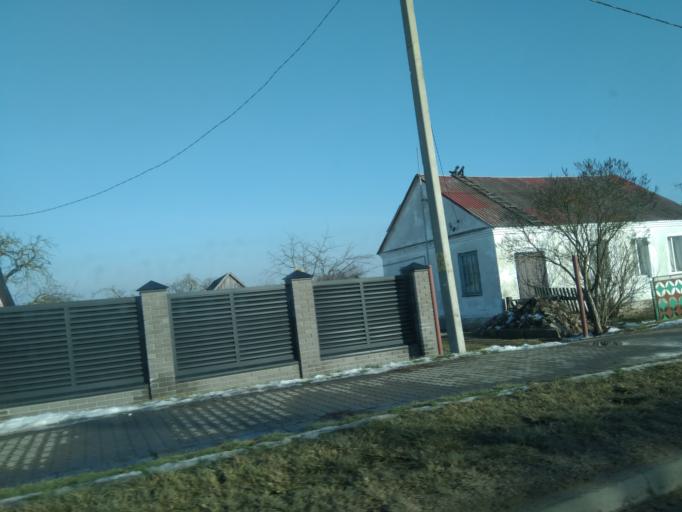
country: BY
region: Minsk
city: Snow
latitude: 53.2234
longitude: 26.3982
